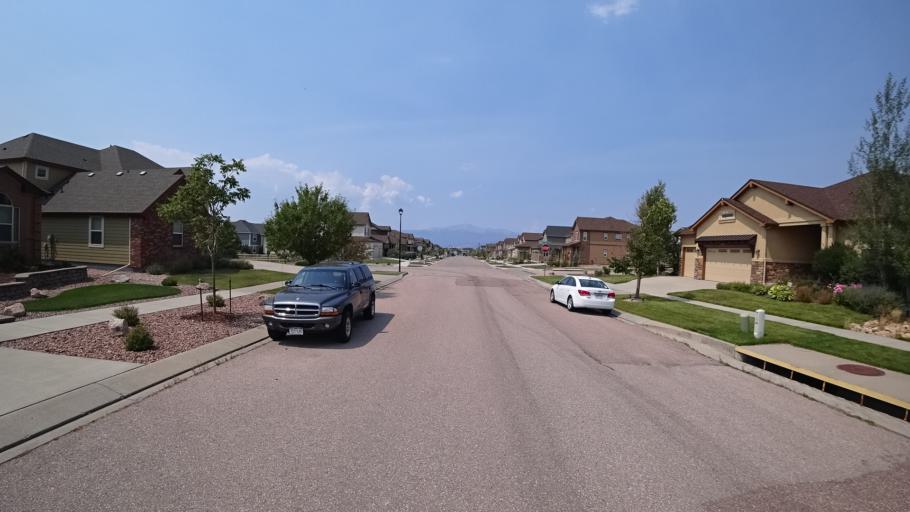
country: US
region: Colorado
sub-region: El Paso County
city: Black Forest
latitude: 38.9679
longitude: -104.7218
